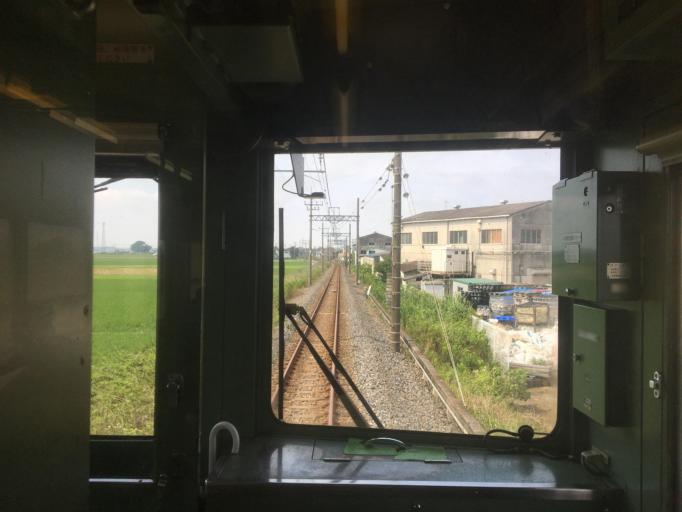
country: JP
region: Tochigi
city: Sano
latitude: 36.2946
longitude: 139.5682
